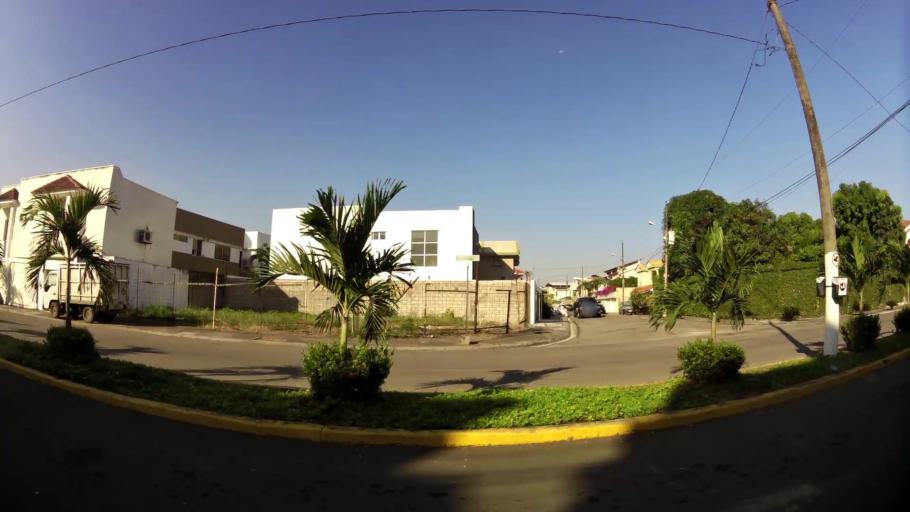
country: EC
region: Guayas
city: Santa Lucia
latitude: -2.1931
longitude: -79.9714
